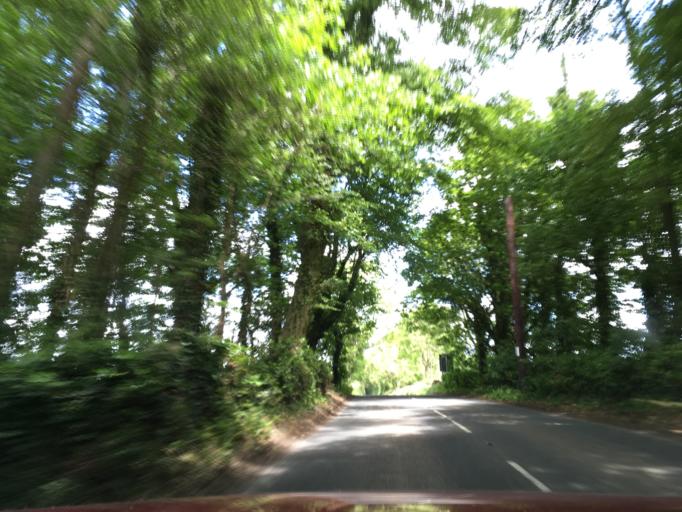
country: GB
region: England
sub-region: Gloucestershire
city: Chalford
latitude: 51.7884
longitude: -2.1291
